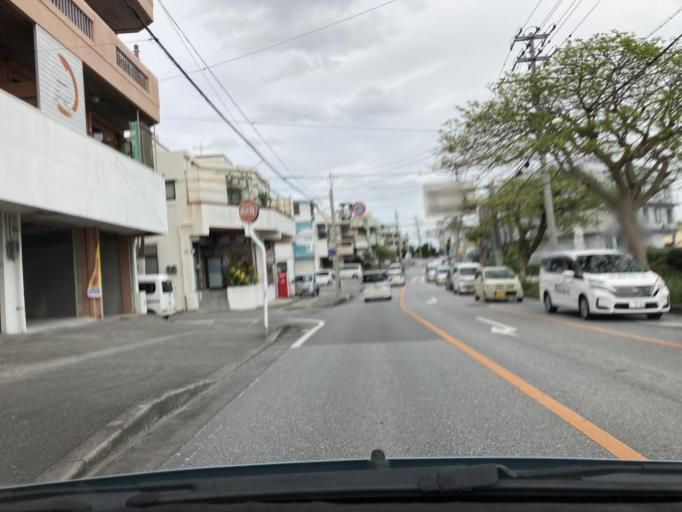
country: JP
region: Okinawa
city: Tomigusuku
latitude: 26.1820
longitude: 127.6812
